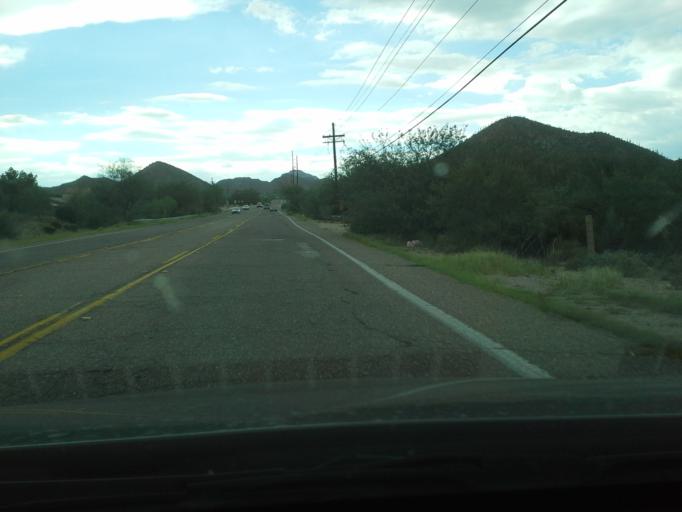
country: US
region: Arizona
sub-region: Pima County
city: South Tucson
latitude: 32.2069
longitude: -111.0173
